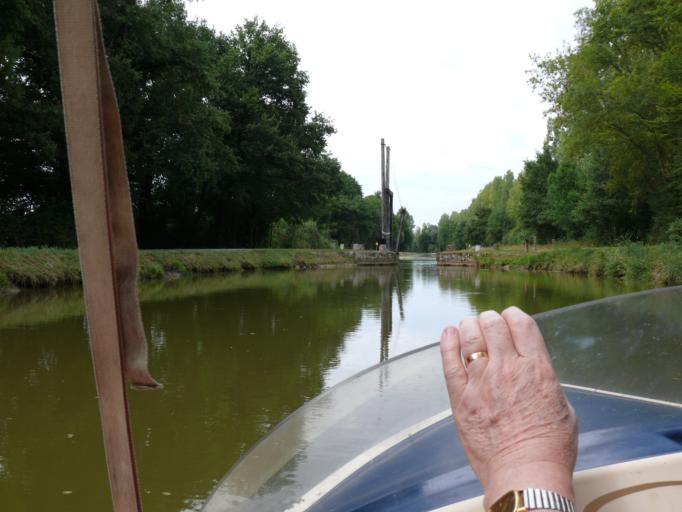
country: FR
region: Auvergne
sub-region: Departement de l'Allier
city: Vallon-en-Sully
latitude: 46.5183
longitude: 2.6145
